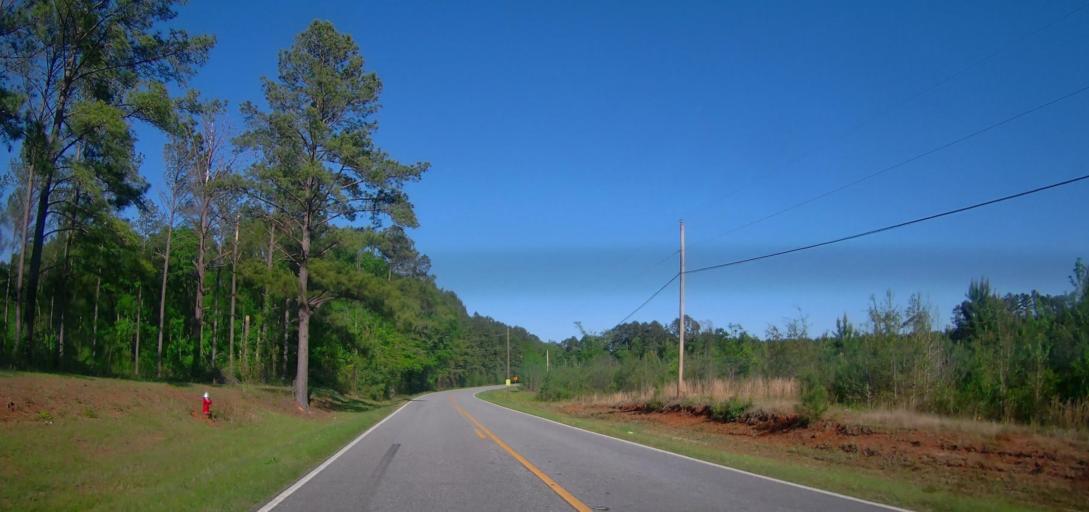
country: US
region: Georgia
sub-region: Houston County
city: Perry
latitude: 32.4504
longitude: -83.6297
